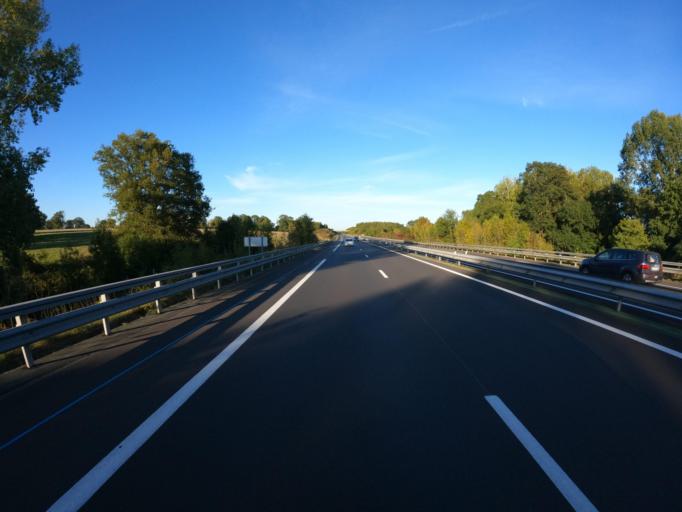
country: FR
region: Pays de la Loire
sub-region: Departement de la Vendee
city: Beaurepaire
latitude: 46.8812
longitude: -1.1075
